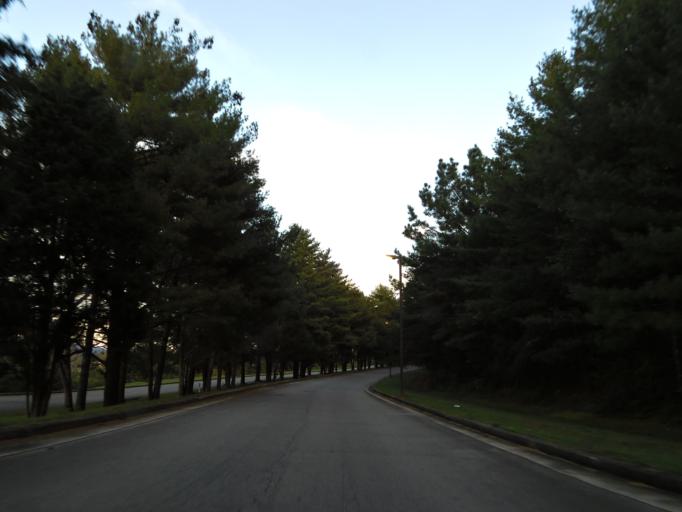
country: US
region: Tennessee
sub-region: Blount County
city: Eagleton Village
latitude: 35.8623
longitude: -83.9438
